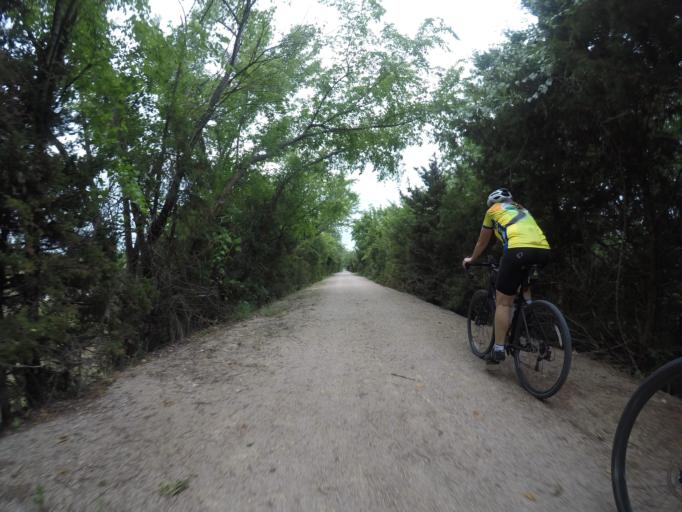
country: US
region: Kansas
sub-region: Anderson County
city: Garnett
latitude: 38.2942
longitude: -95.2430
